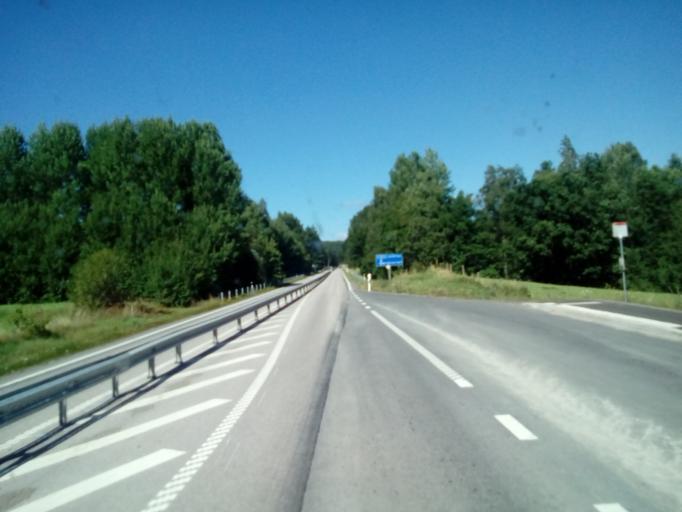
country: SE
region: OEstergoetland
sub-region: Kinda Kommun
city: Rimforsa
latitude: 58.0692
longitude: 15.6561
